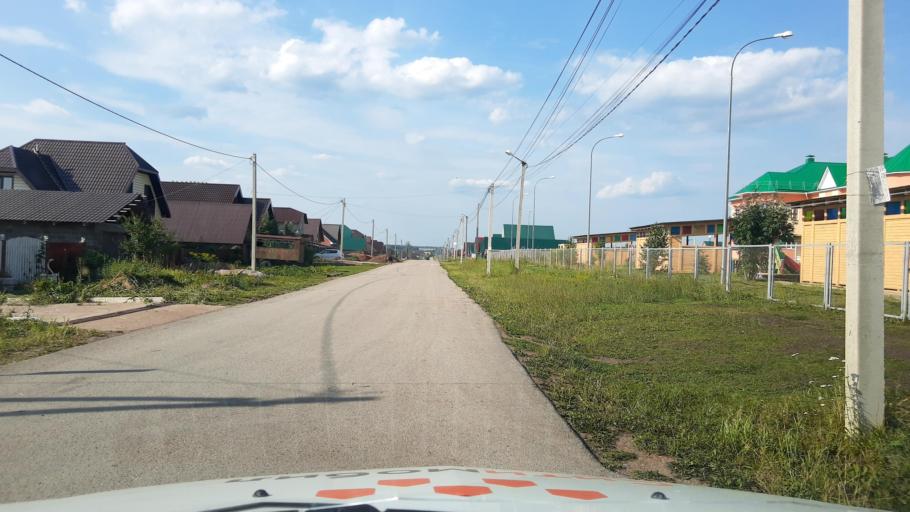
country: RU
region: Bashkortostan
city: Kabakovo
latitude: 54.6524
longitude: 56.2126
